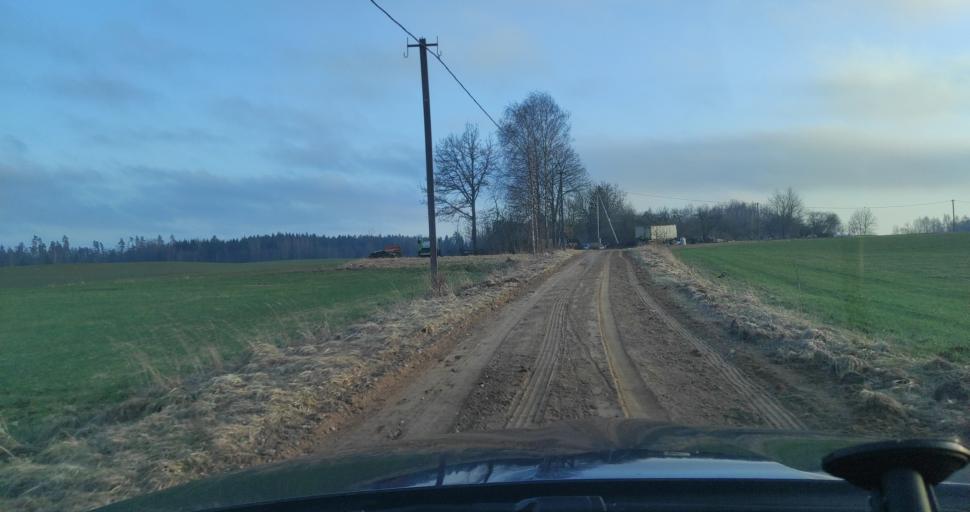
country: LV
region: Aizpute
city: Aizpute
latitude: 56.8009
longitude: 21.8044
